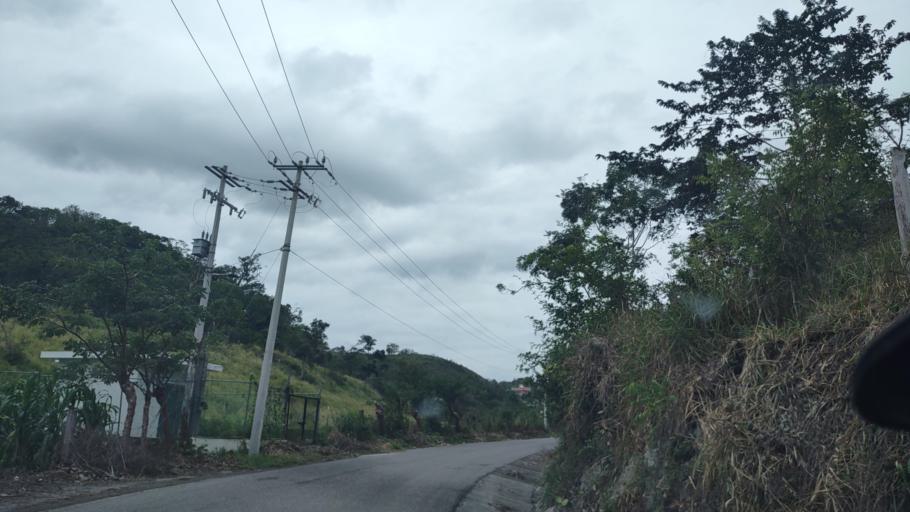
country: MX
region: Veracruz
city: Papantla de Olarte
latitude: 20.4424
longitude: -97.2996
